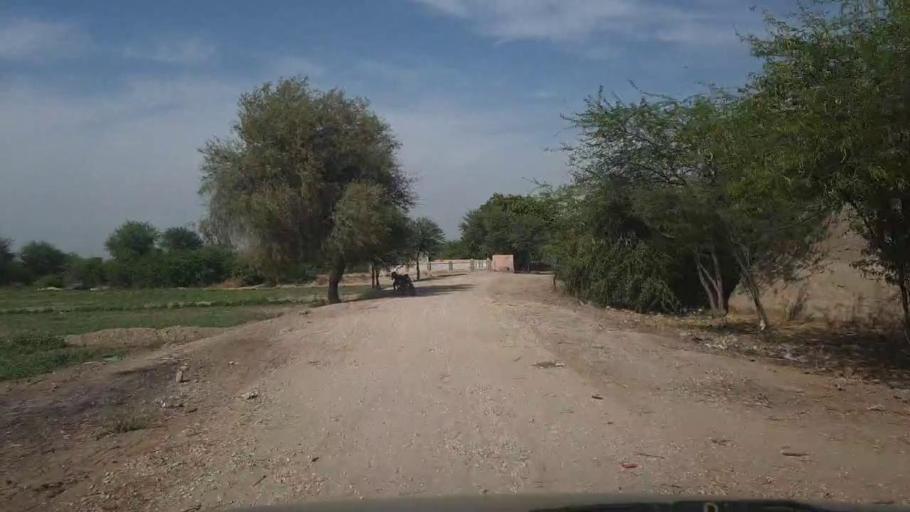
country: PK
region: Sindh
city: Nabisar
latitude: 25.1638
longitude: 69.6681
